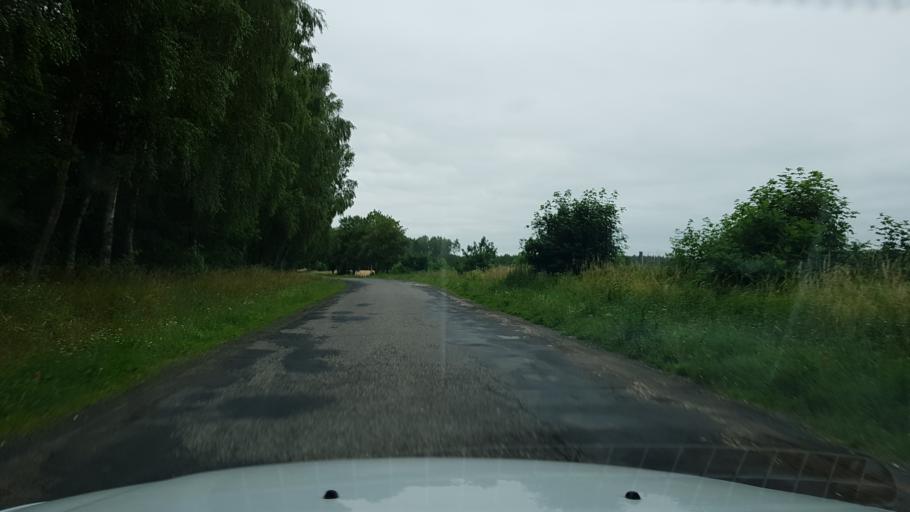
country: PL
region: West Pomeranian Voivodeship
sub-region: Powiat gryficki
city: Brojce
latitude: 53.9484
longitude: 15.3878
